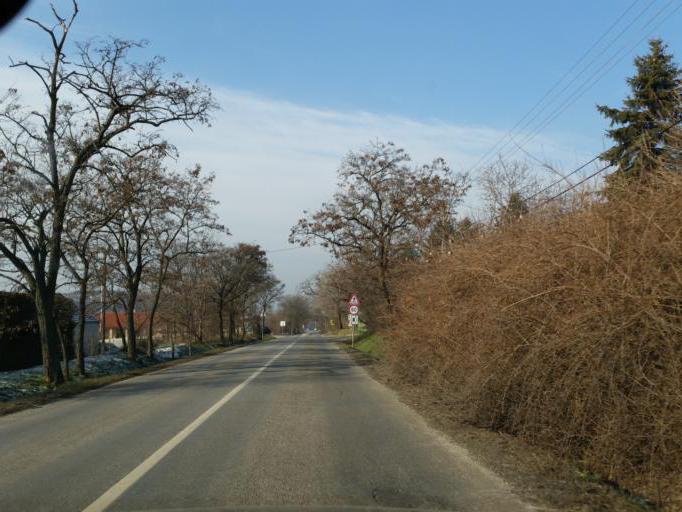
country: HU
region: Pest
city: Telki
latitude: 47.5519
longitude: 18.8150
